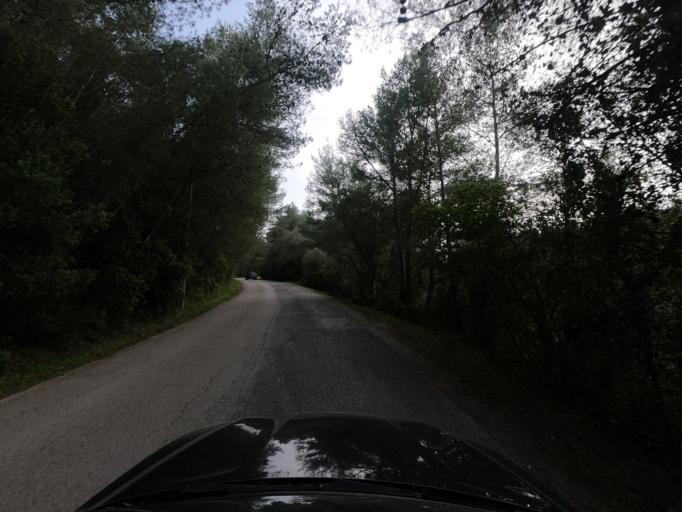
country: PT
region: Setubal
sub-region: Setubal
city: Setubal
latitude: 38.5200
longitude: -8.9082
